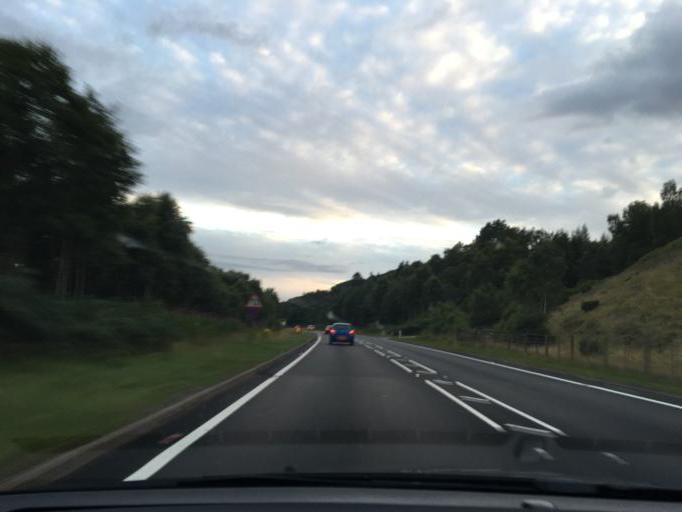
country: GB
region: Scotland
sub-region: Highland
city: Aviemore
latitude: 57.2309
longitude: -3.8145
